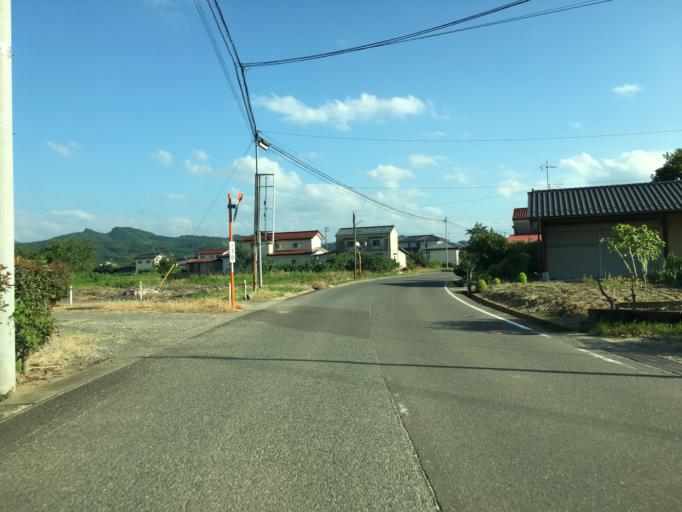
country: JP
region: Fukushima
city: Yanagawamachi-saiwaicho
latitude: 37.8363
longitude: 140.5845
